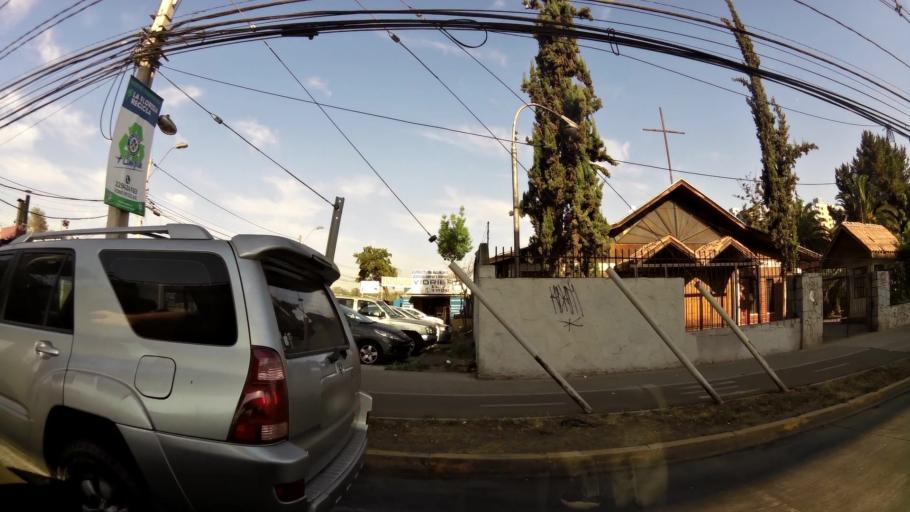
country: CL
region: Santiago Metropolitan
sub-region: Provincia de Santiago
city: La Pintana
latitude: -33.5529
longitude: -70.5869
